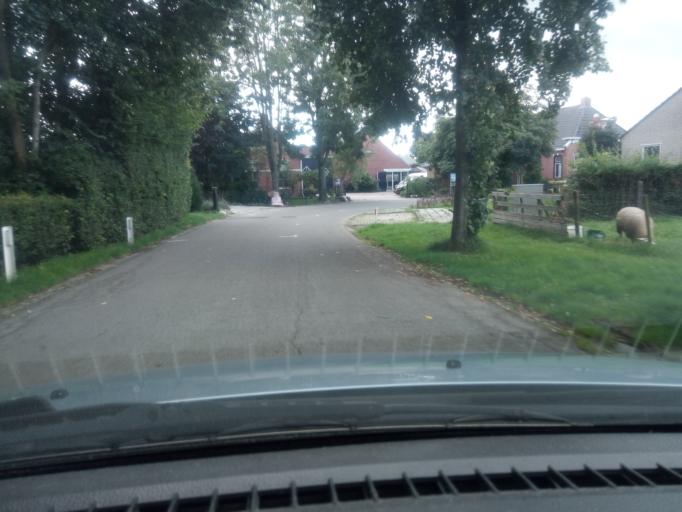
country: NL
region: Groningen
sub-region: Gemeente Zuidhorn
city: Grijpskerk
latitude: 53.2650
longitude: 6.2514
